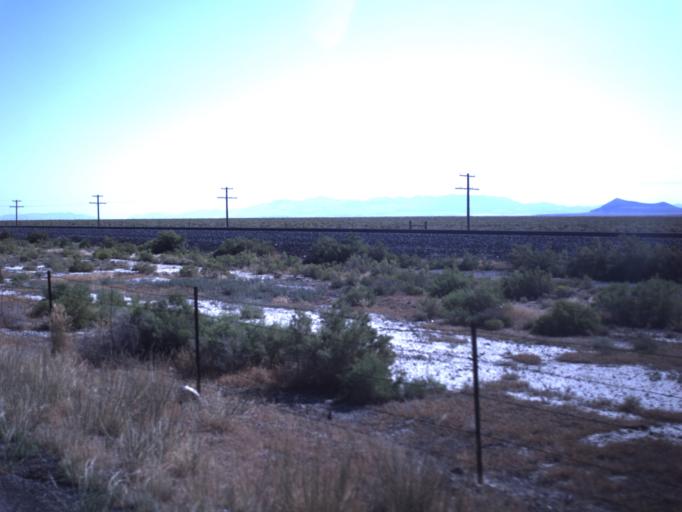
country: US
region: Utah
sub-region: Millard County
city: Delta
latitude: 39.0789
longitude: -112.7560
